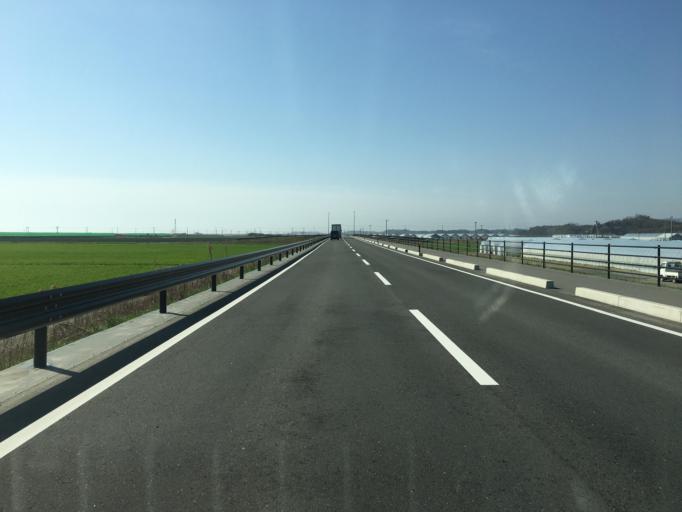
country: JP
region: Miyagi
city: Watari
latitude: 37.9526
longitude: 140.9054
